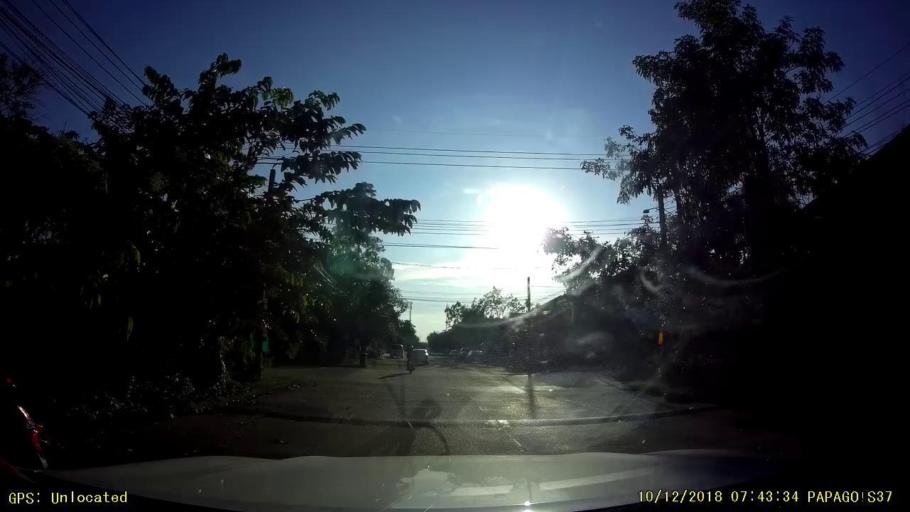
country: TH
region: Bangkok
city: Lat Krabang
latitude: 13.7919
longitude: 100.8142
